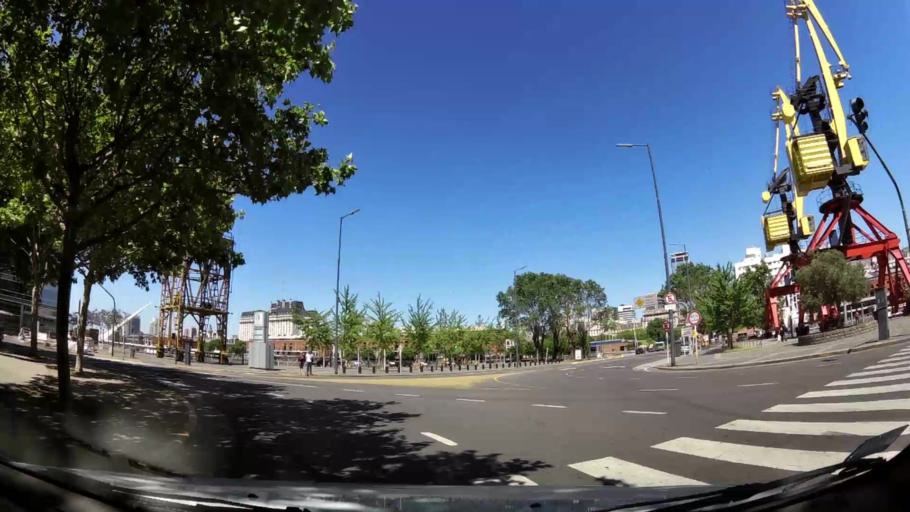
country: AR
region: Buenos Aires F.D.
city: Buenos Aires
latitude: -34.6049
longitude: -58.3644
